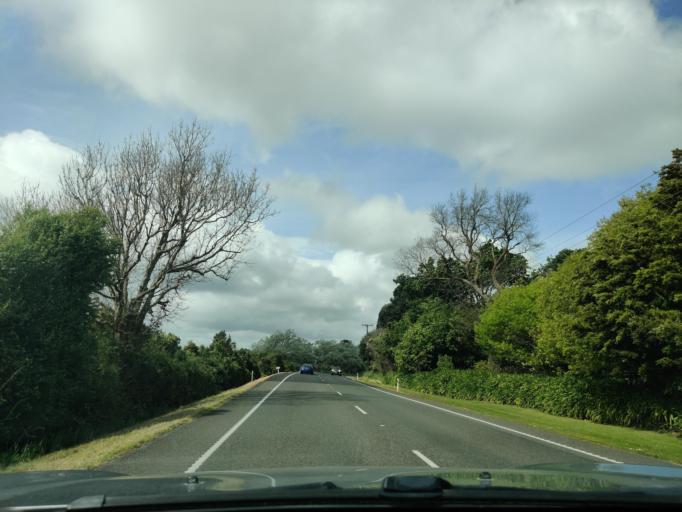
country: NZ
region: Taranaki
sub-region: South Taranaki District
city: Patea
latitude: -39.8077
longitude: 174.7569
